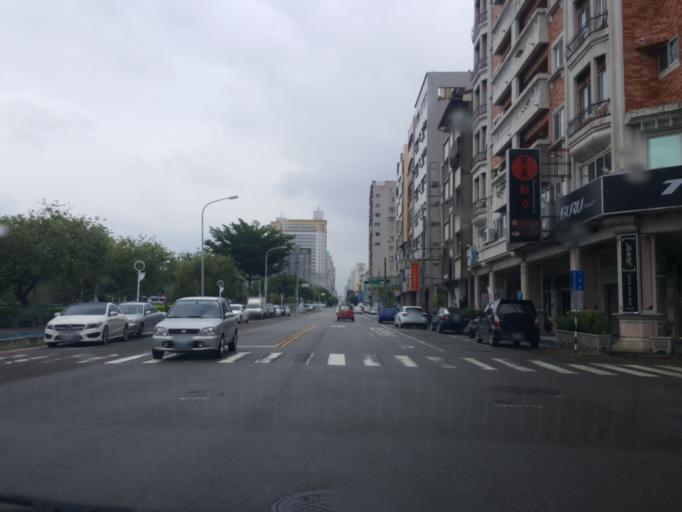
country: TW
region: Taiwan
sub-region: Taichung City
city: Taichung
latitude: 24.1368
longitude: 120.6683
